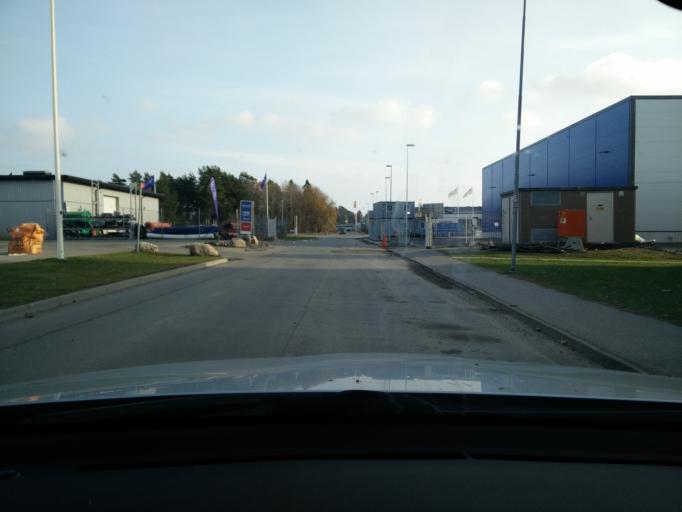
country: SE
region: Stockholm
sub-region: Taby Kommun
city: Taby
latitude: 59.4675
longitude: 18.1255
